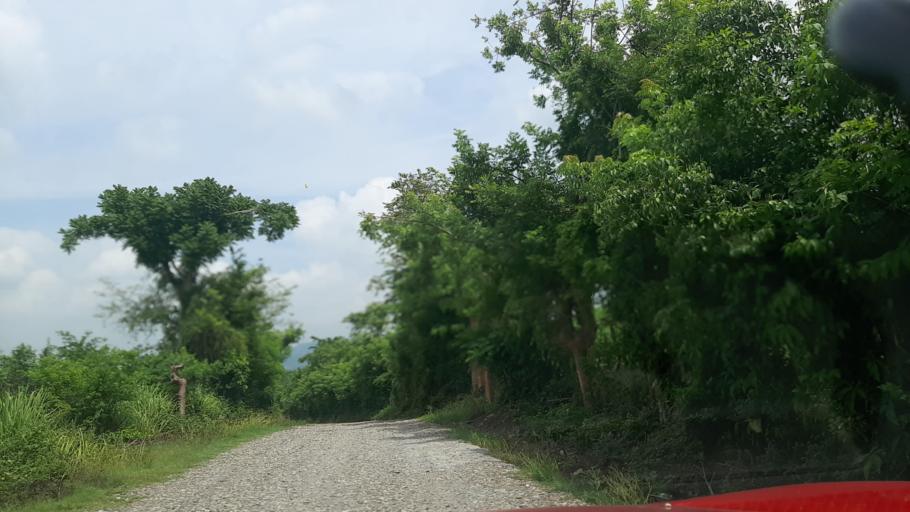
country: MX
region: Veracruz
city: Gutierrez Zamora
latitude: 20.4456
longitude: -97.1730
